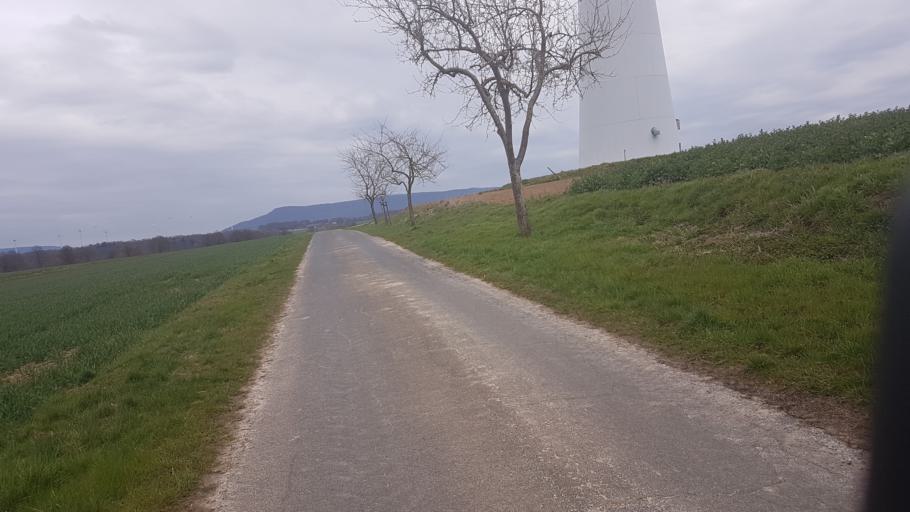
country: DE
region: Lower Saxony
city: Bad Munder am Deister
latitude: 52.1345
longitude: 9.4325
